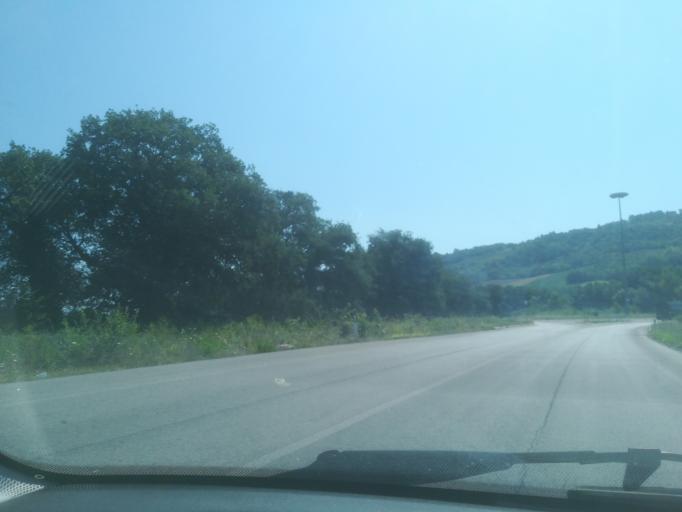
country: IT
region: The Marches
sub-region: Provincia di Macerata
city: Villa Potenza
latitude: 43.3337
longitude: 13.4376
